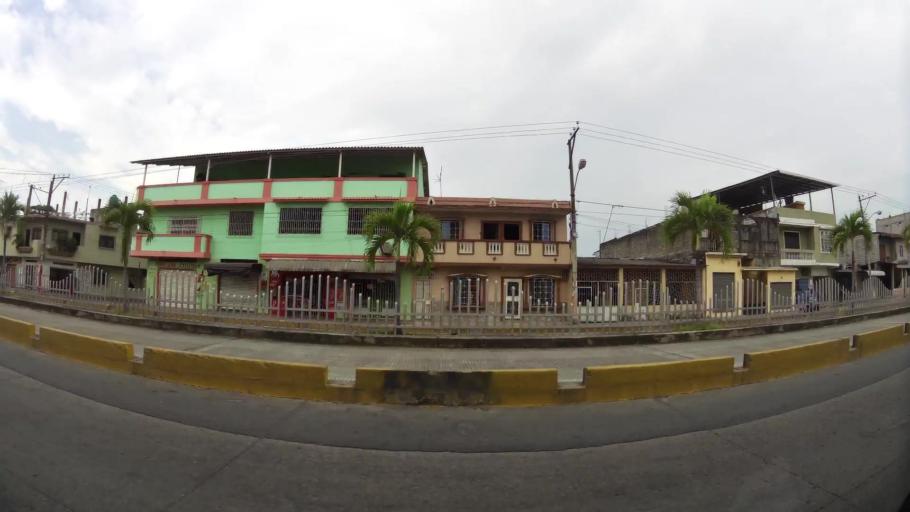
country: EC
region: Guayas
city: Guayaquil
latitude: -2.2564
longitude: -79.8793
